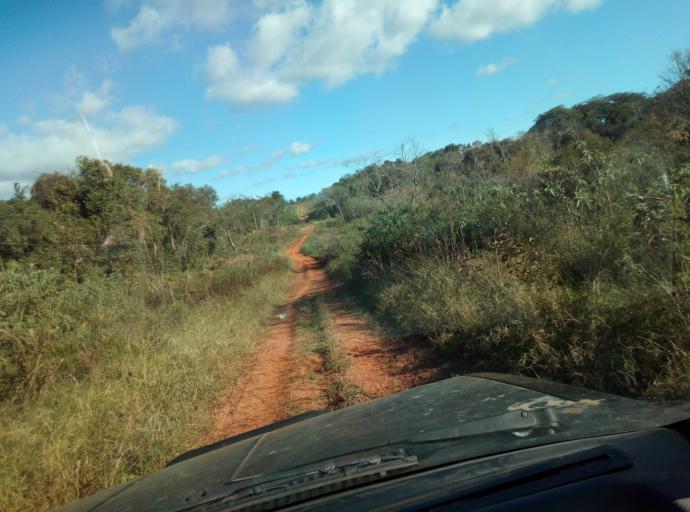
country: PY
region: Caaguazu
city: Carayao
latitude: -25.1709
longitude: -56.2731
